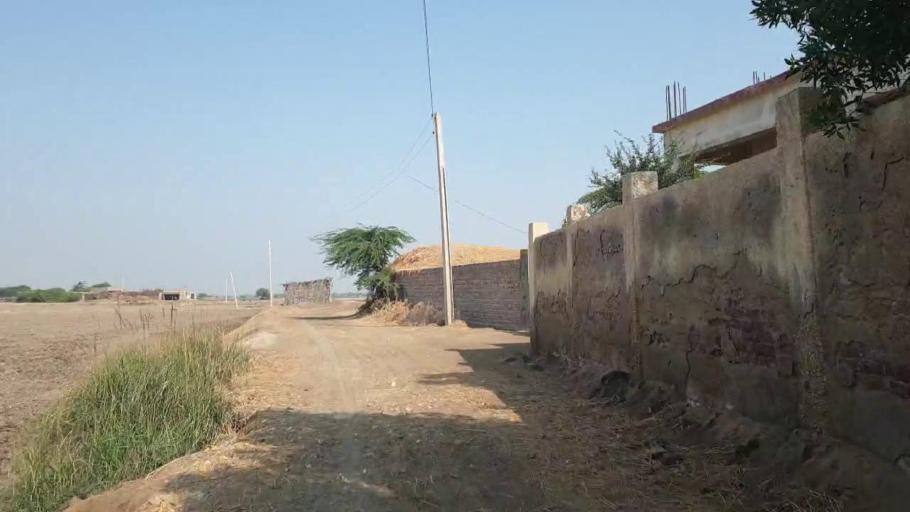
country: PK
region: Sindh
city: Matli
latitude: 24.9786
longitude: 68.5900
